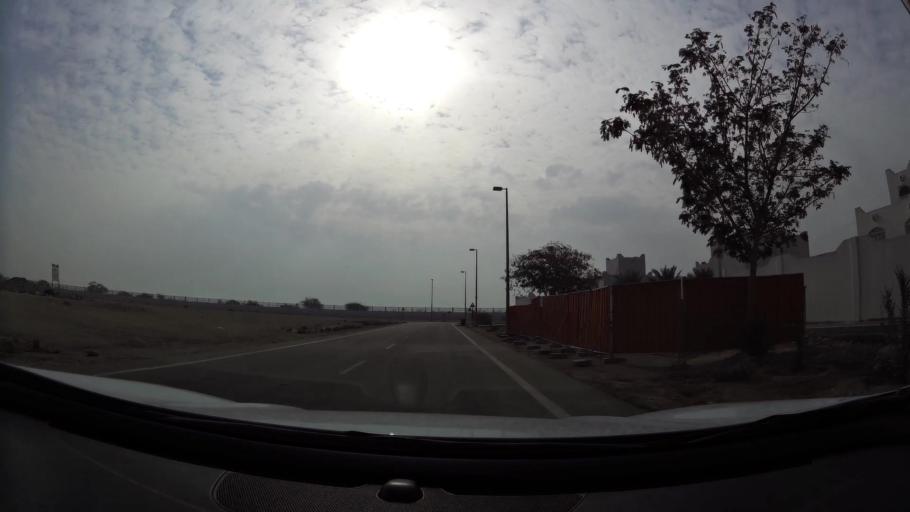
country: AE
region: Abu Dhabi
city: Abu Dhabi
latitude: 24.6698
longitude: 54.7760
